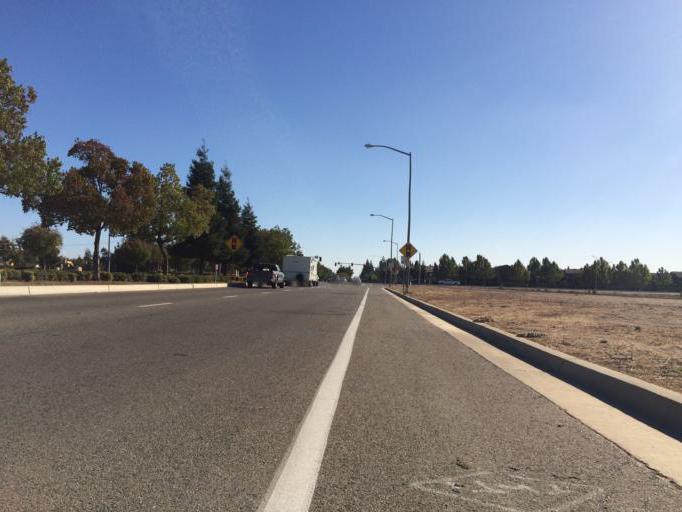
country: US
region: California
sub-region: Fresno County
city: Clovis
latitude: 36.8390
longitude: -119.6642
